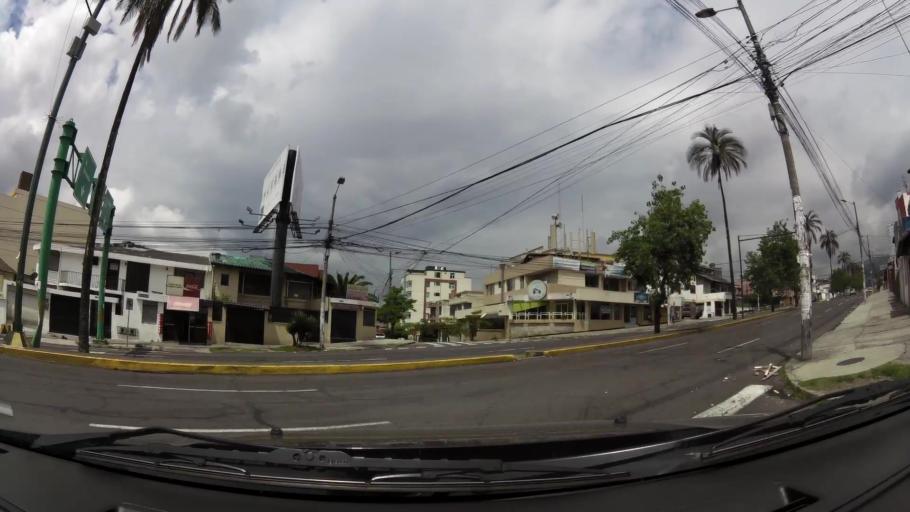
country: EC
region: Pichincha
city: Quito
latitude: -0.1847
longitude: -78.4930
